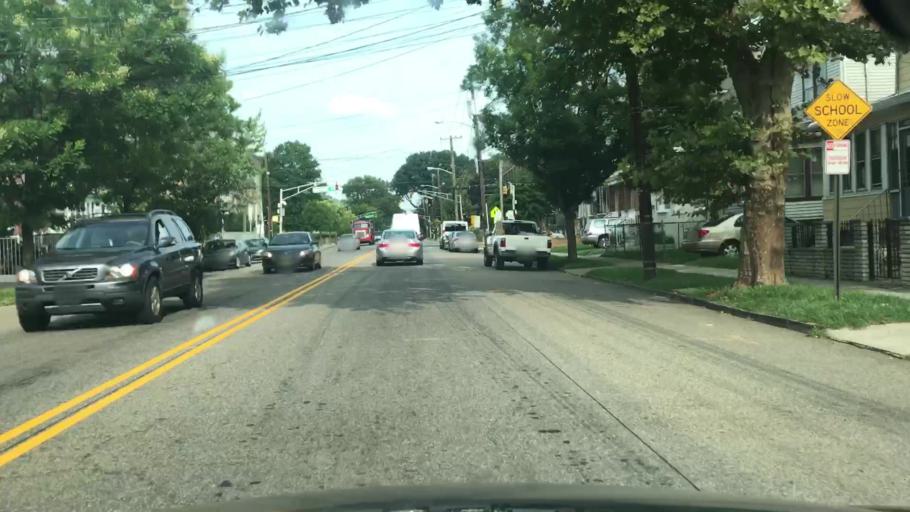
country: US
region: New Jersey
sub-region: Union County
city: Elizabeth
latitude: 40.6791
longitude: -74.2011
